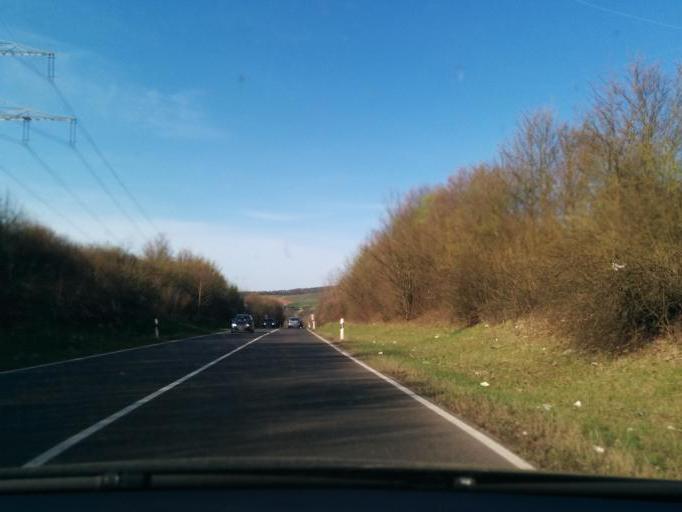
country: DE
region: Rheinland-Pfalz
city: Windesheim
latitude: 49.8936
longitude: 7.8197
